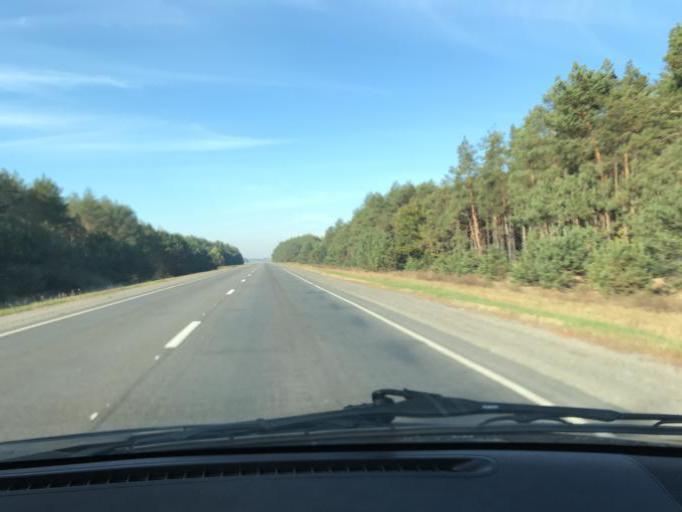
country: BY
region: Brest
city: Davyd-Haradok
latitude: 52.2383
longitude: 27.2188
